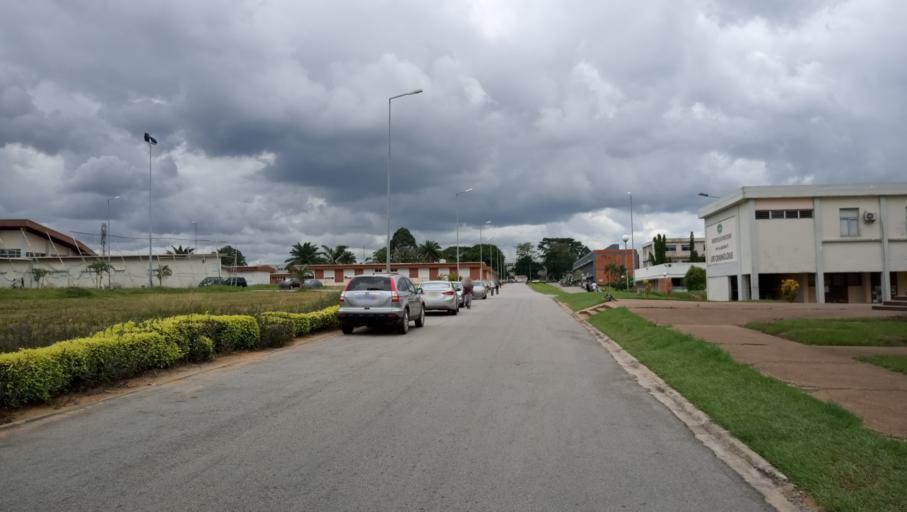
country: CI
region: Lagunes
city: Abidjan
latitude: 5.3396
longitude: -3.9867
